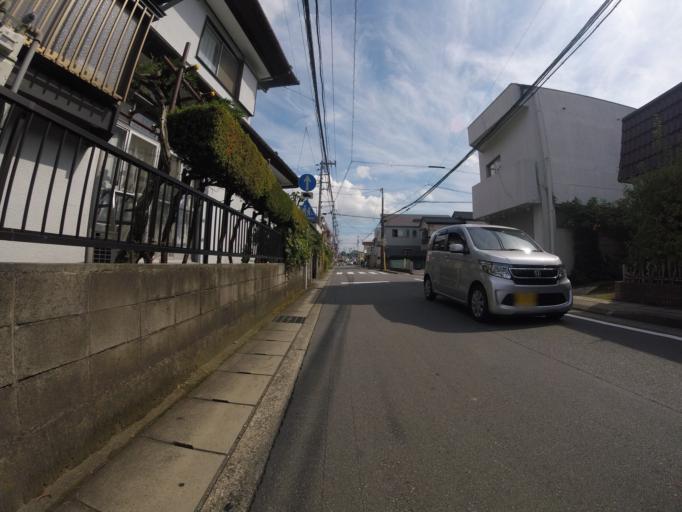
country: JP
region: Shizuoka
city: Mishima
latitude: 35.1177
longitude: 138.9311
